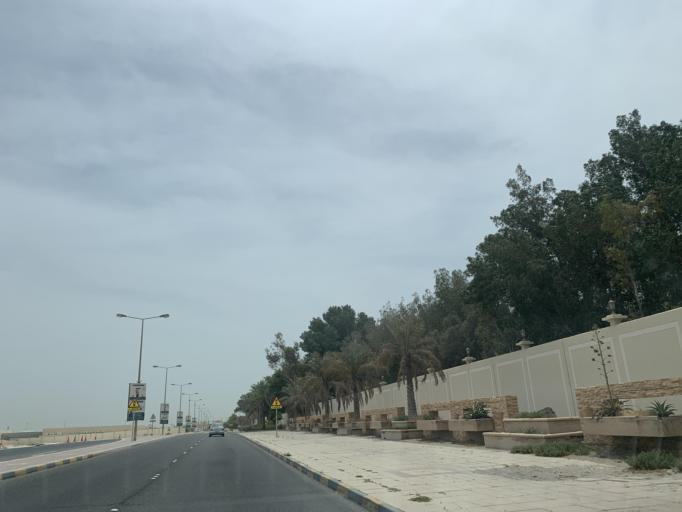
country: BH
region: Northern
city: Ar Rifa'
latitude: 26.1411
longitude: 50.5472
